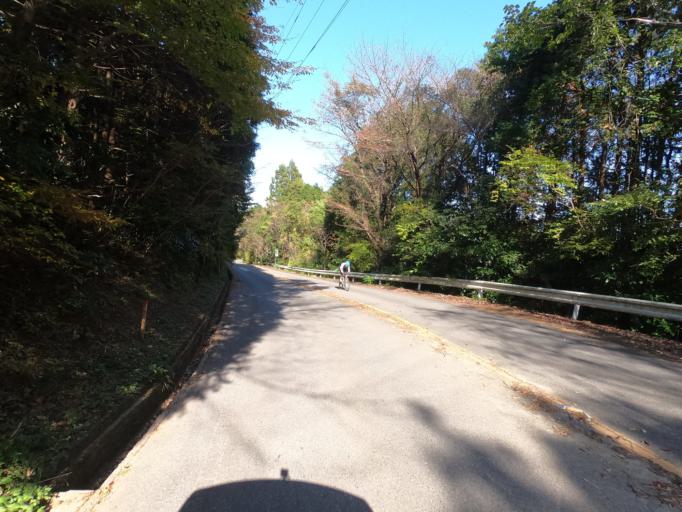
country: JP
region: Ibaraki
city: Tsukuba
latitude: 36.2239
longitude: 140.1262
